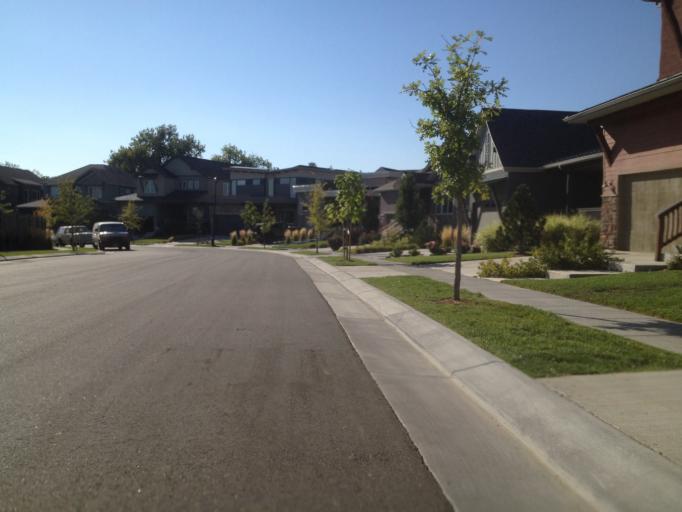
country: US
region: Colorado
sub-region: Boulder County
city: Louisville
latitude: 39.9896
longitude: -105.1206
